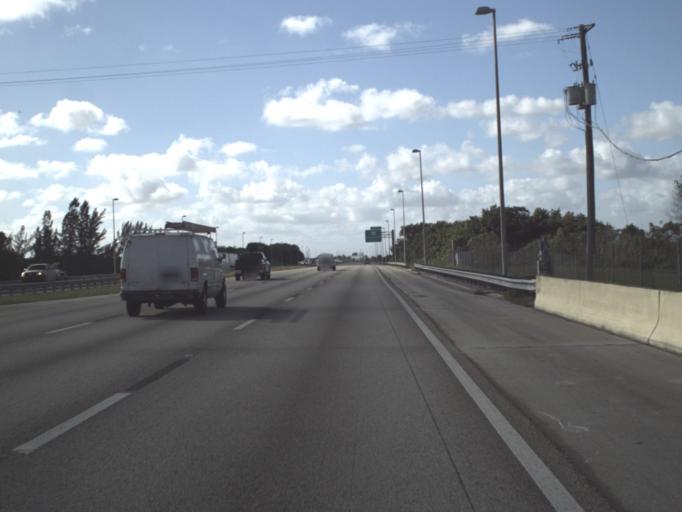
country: US
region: Florida
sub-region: Broward County
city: Coral Springs
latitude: 26.2878
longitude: -80.2973
